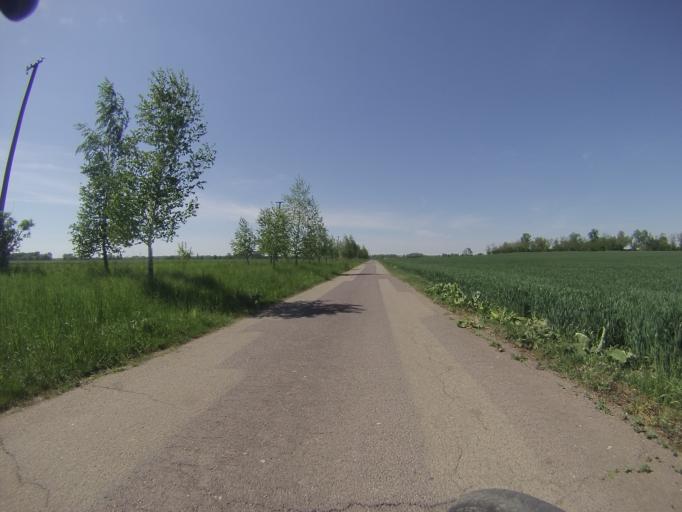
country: CZ
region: South Moravian
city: Novosedly
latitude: 48.8111
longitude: 16.4824
